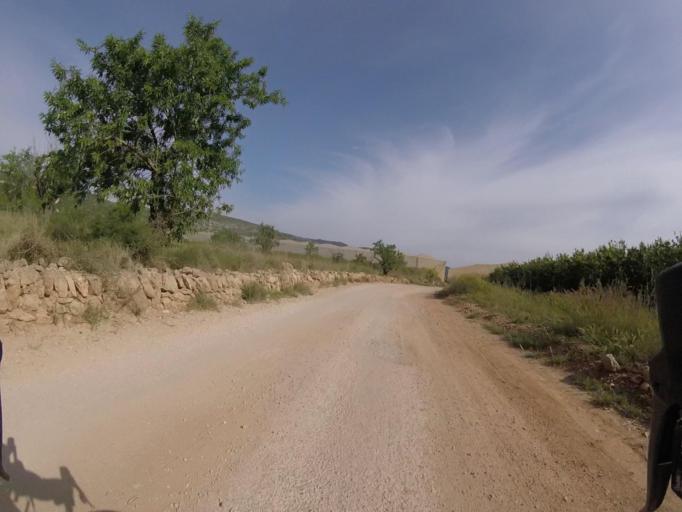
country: ES
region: Valencia
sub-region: Provincia de Castello
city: Alcala de Xivert
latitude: 40.2773
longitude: 0.2582
